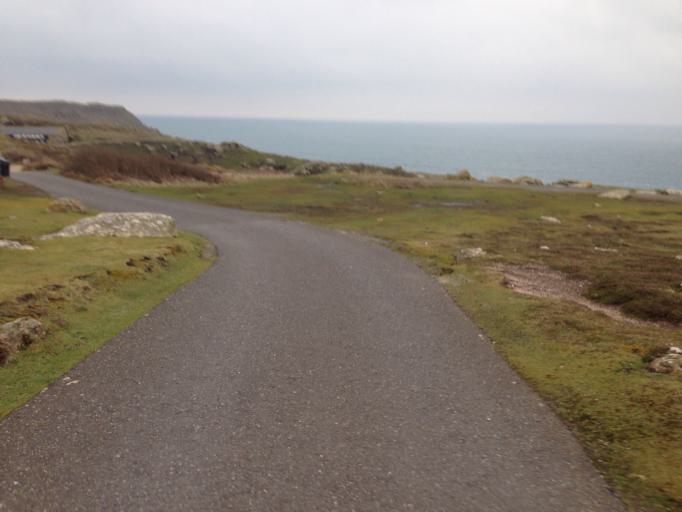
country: GB
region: England
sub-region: Cornwall
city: Sennen
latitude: 50.0644
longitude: -5.7121
